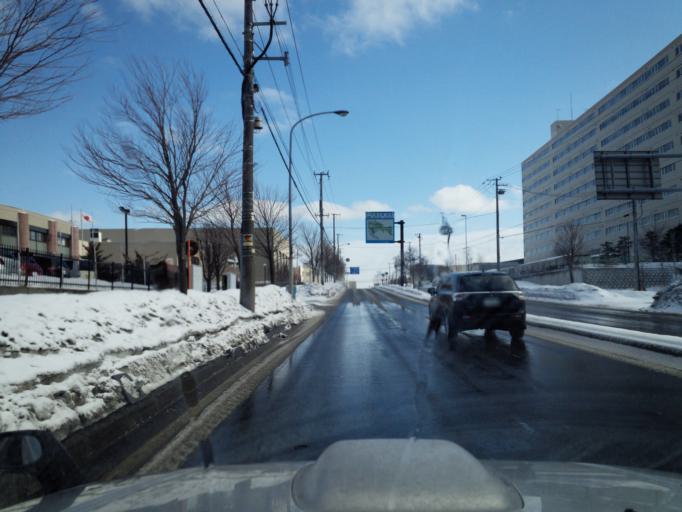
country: JP
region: Hokkaido
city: Kitahiroshima
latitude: 42.9902
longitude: 141.4514
